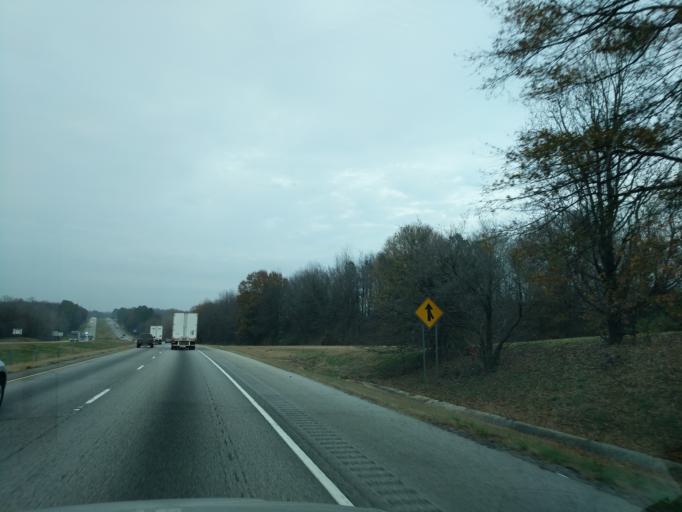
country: US
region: Georgia
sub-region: Franklin County
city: Carnesville
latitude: 34.3734
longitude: -83.2625
